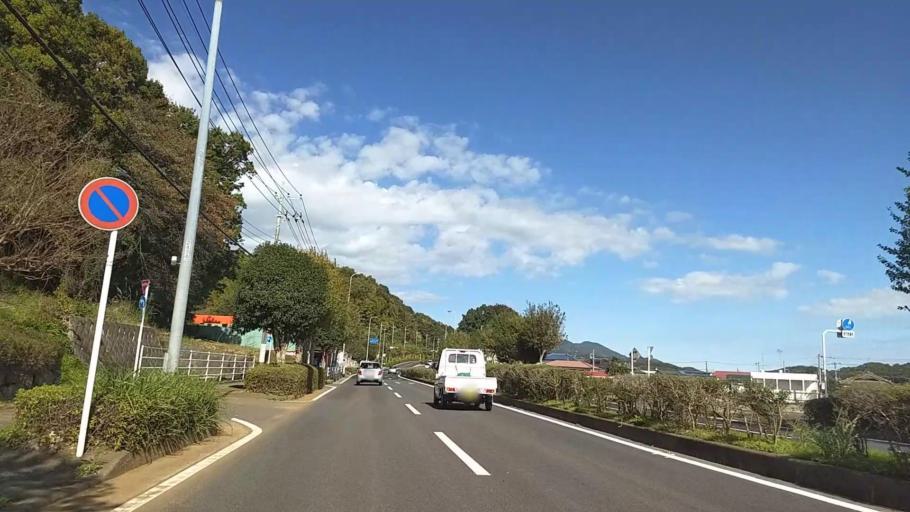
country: JP
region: Kanagawa
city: Hadano
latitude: 35.3417
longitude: 139.2302
